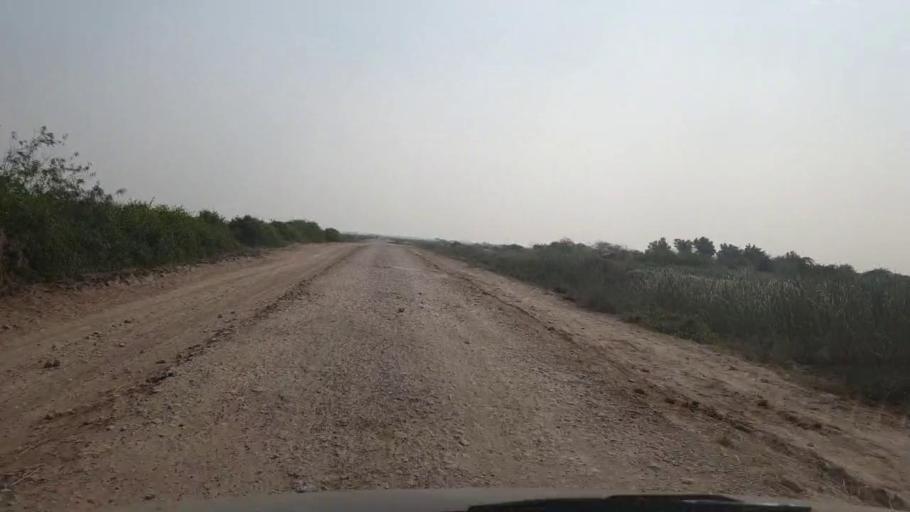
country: PK
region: Sindh
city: Tando Muhammad Khan
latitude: 25.0934
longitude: 68.3819
